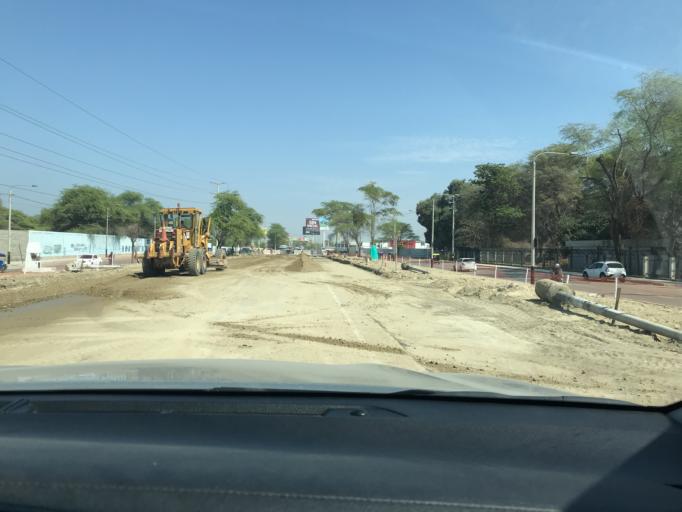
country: PE
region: Piura
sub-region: Provincia de Piura
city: Piura
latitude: -5.1807
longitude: -80.6604
